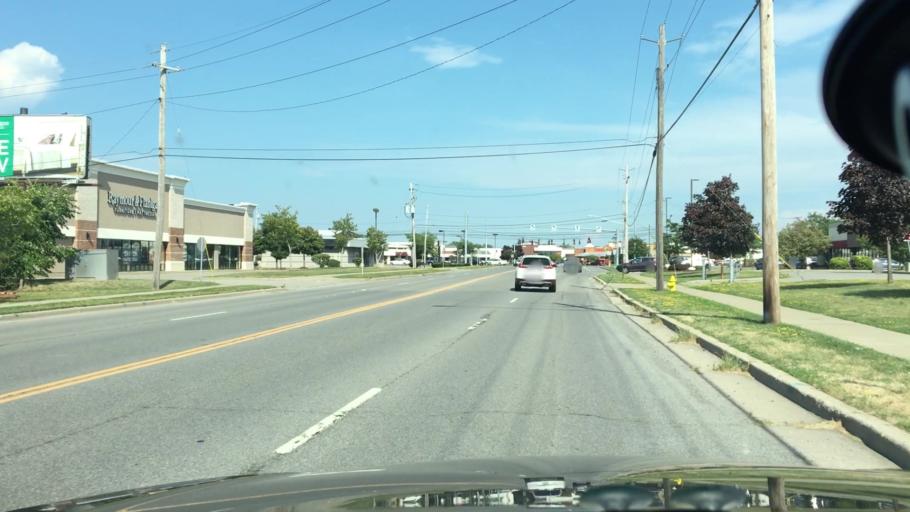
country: US
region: New York
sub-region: Erie County
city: Cheektowaga
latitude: 42.9160
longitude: -78.7566
